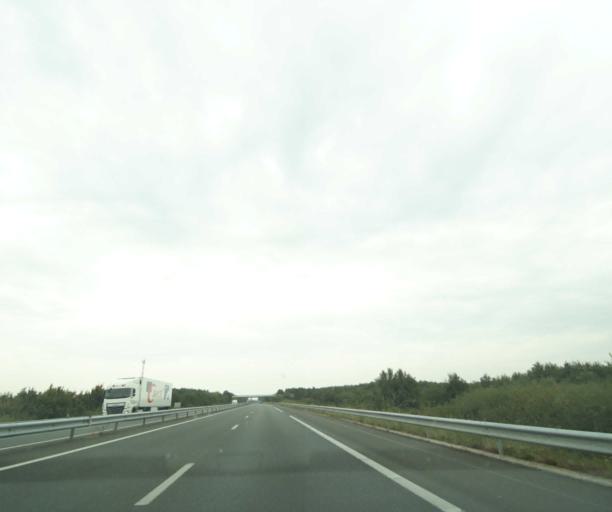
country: FR
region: Pays de la Loire
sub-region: Departement de la Vendee
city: Saint-Martin-des-Noyers
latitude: 46.6884
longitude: -1.1568
